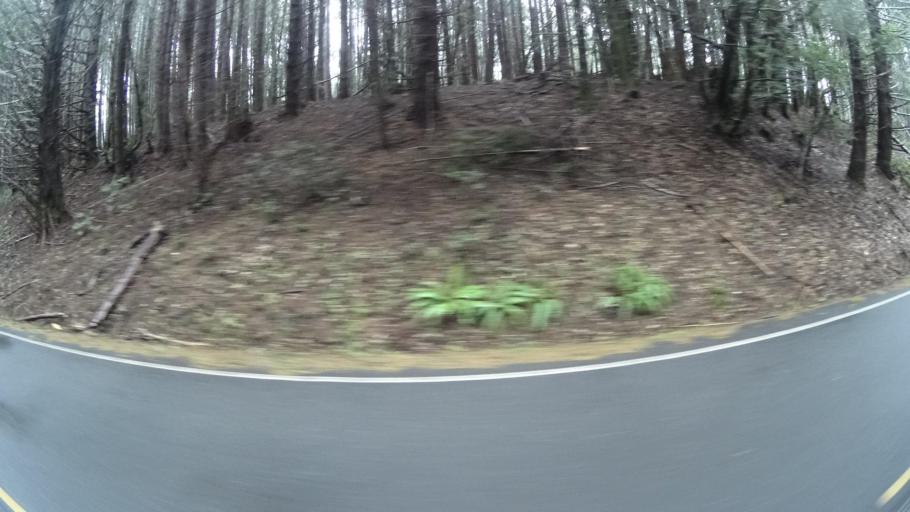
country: US
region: California
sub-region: Humboldt County
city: Westhaven-Moonstone
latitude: 41.2148
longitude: -123.9573
